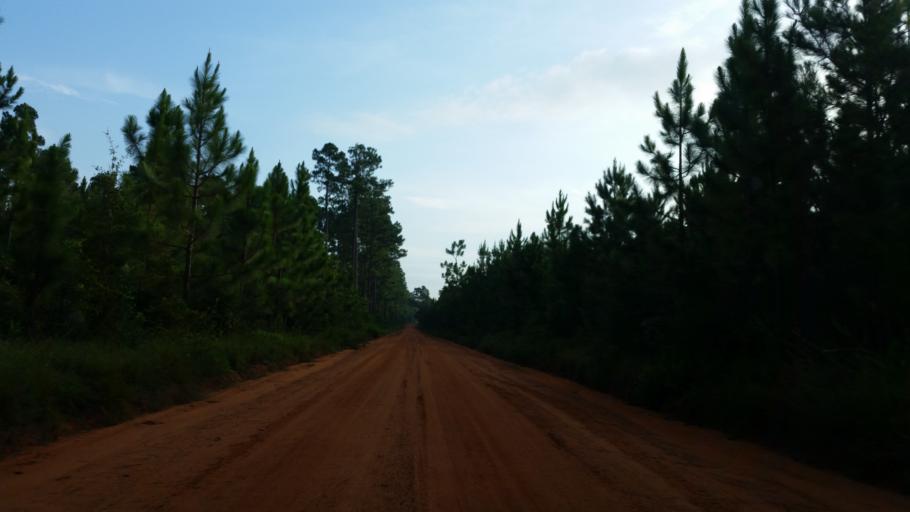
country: US
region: Alabama
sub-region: Escambia County
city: Atmore
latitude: 30.9105
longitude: -87.5816
